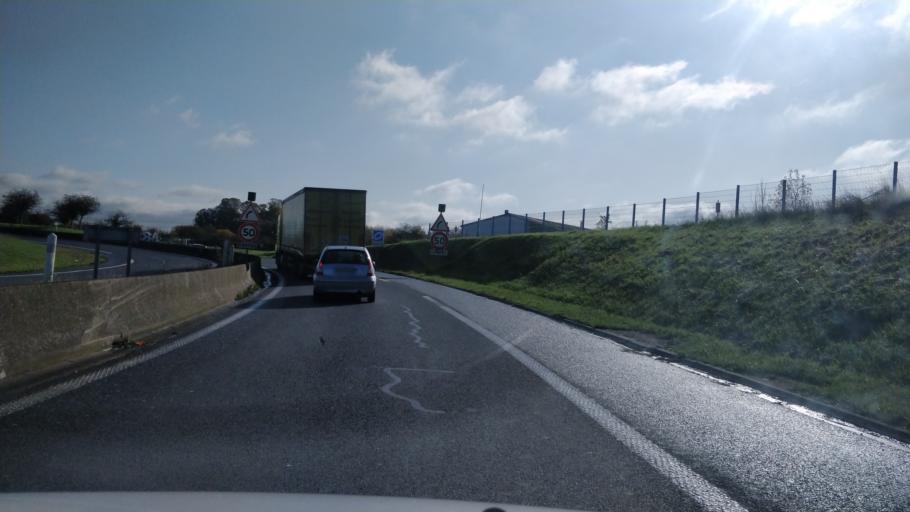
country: FR
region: Lower Normandy
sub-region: Departement du Calvados
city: Bretteville-sur-Odon
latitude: 49.1641
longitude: -0.4300
